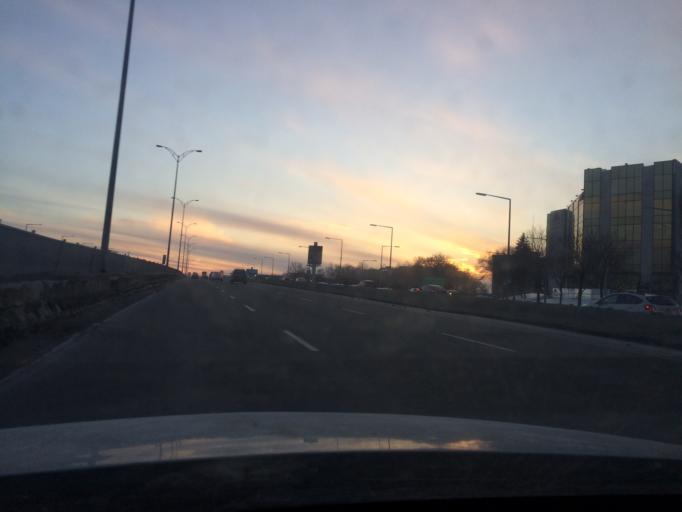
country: CA
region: Quebec
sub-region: Montreal
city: Saint-Leonard
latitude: 45.5952
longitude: -73.5758
